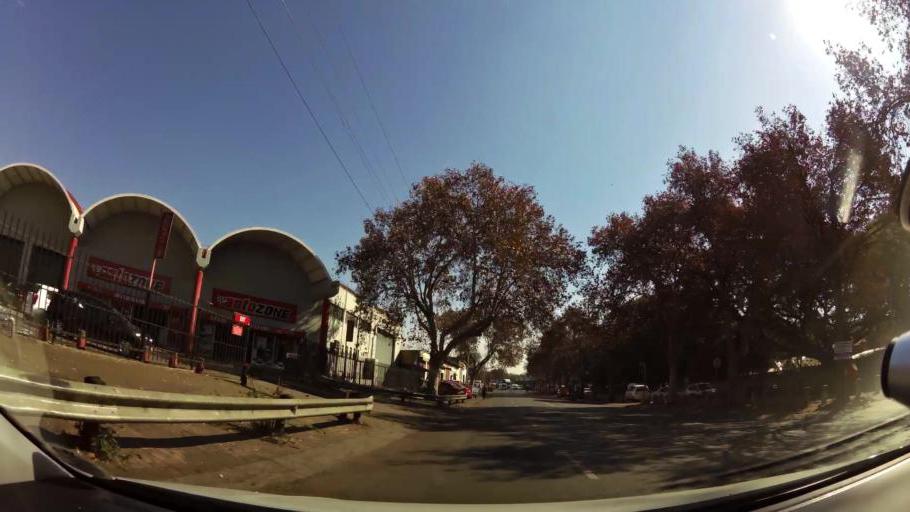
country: ZA
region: Gauteng
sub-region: City of Tshwane Metropolitan Municipality
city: Pretoria
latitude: -25.7409
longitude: 28.1964
